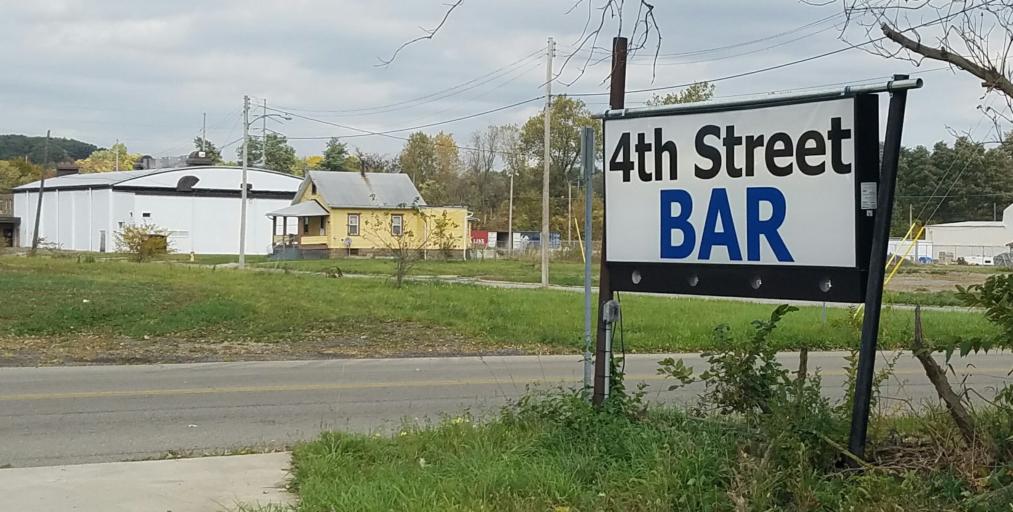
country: US
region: Ohio
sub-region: Richland County
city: Mansfield
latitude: 40.7605
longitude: -82.5048
